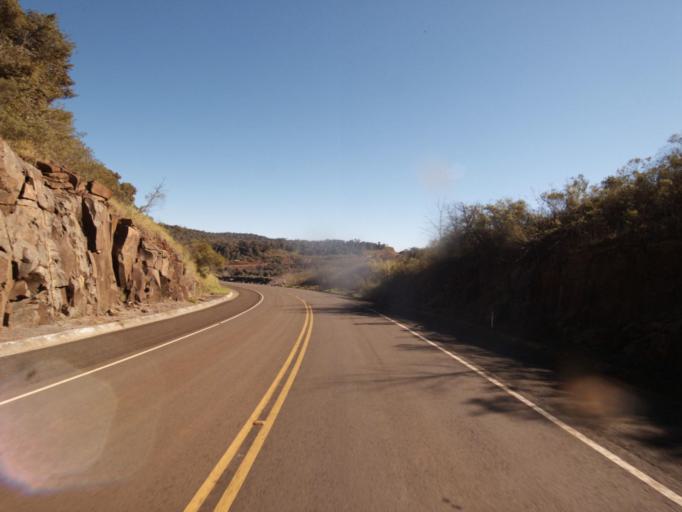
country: AR
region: Misiones
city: Bernardo de Irigoyen
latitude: -26.6092
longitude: -53.7283
